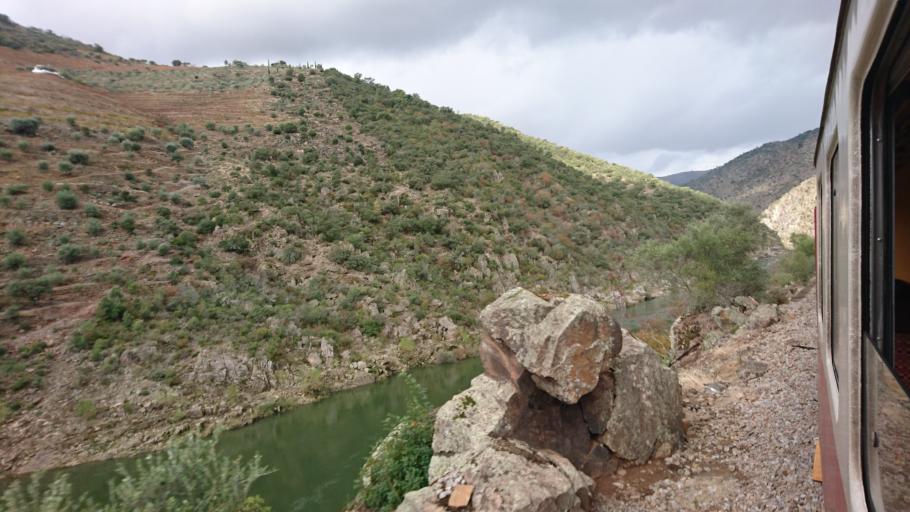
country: PT
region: Viseu
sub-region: Sao Joao da Pesqueira
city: Sao Joao da Pesqueira
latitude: 41.1856
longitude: -7.3858
